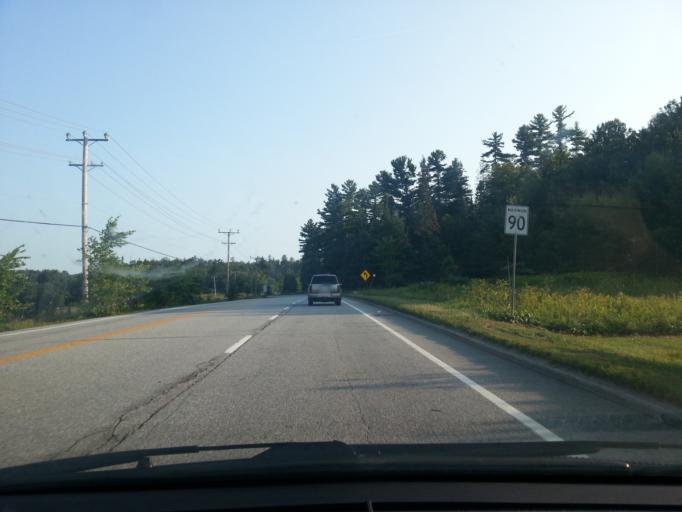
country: CA
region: Quebec
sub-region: Outaouais
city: Wakefield
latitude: 45.8172
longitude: -75.9530
